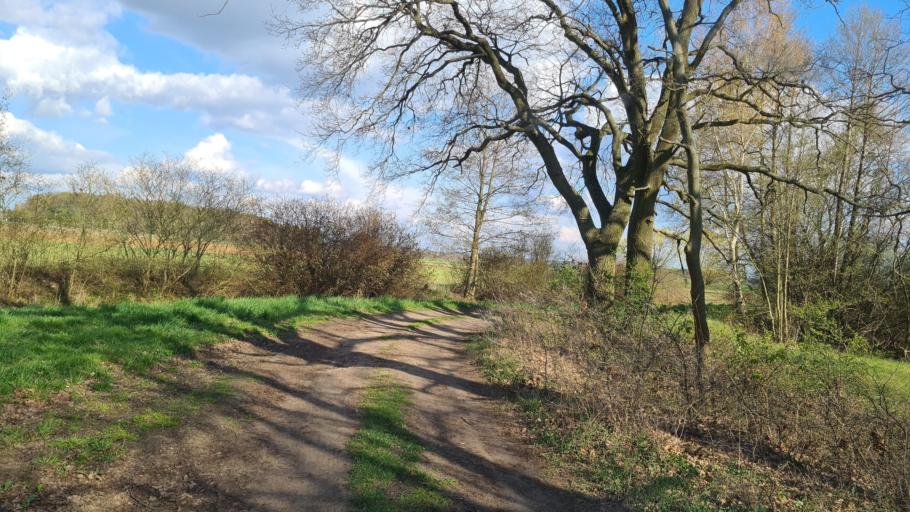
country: DE
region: Brandenburg
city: Herzberg
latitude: 51.6815
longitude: 13.2559
